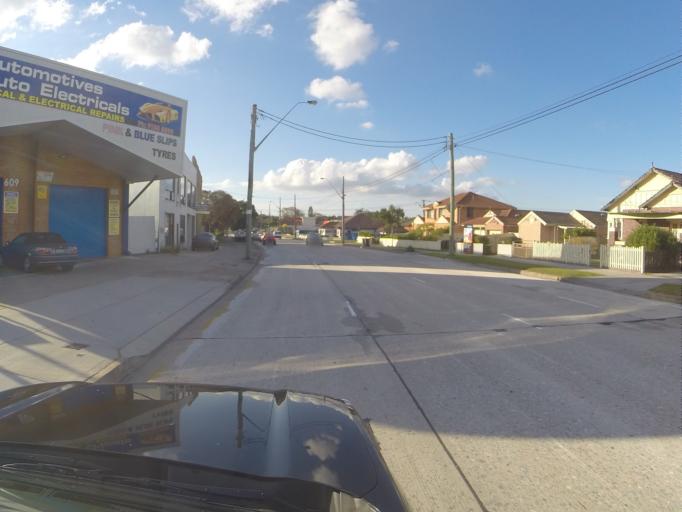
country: AU
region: New South Wales
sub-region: Rockdale
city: Bexley
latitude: -33.9554
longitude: 151.1187
